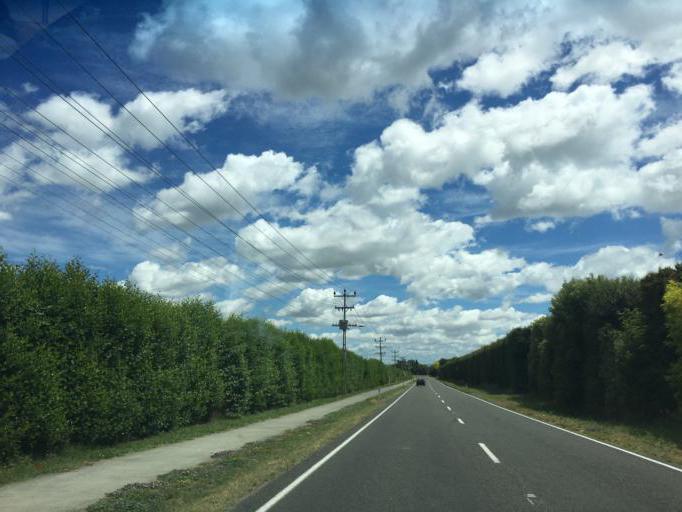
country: NZ
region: Hawke's Bay
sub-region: Hastings District
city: Hastings
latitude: -39.6604
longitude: 176.8818
